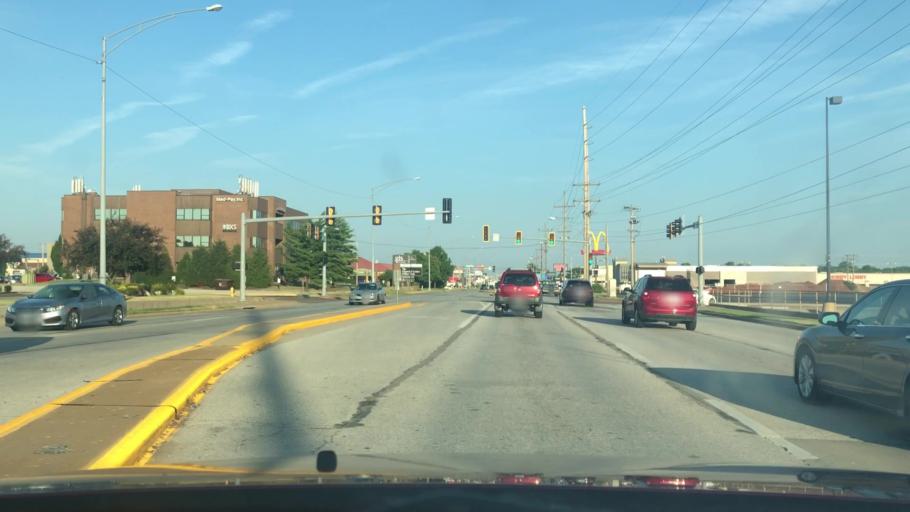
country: US
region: Missouri
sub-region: Greene County
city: Springfield
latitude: 37.1594
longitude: -93.2646
